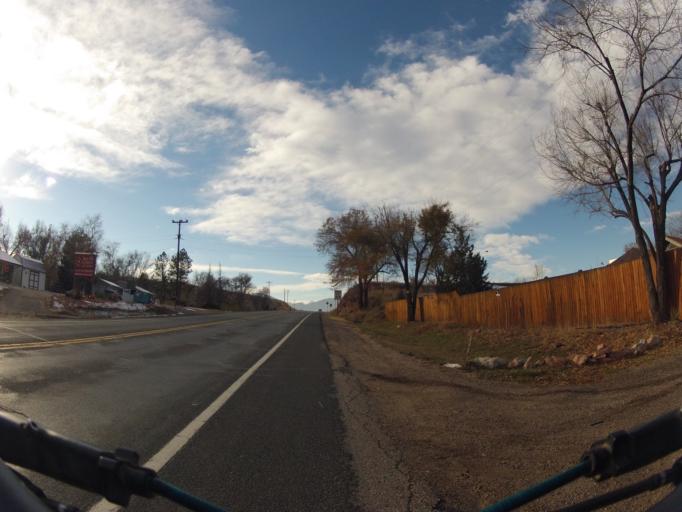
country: US
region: Colorado
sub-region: Larimer County
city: Loveland
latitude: 40.4071
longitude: -105.1465
